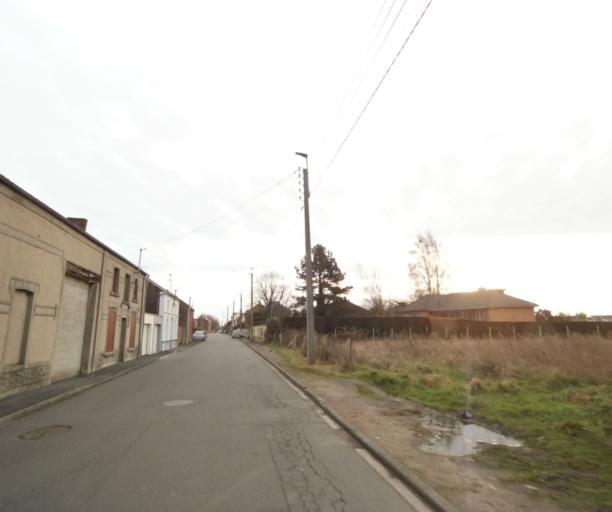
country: FR
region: Nord-Pas-de-Calais
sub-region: Departement du Nord
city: Conde-sur-l'Escaut
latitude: 50.4711
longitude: 3.5929
